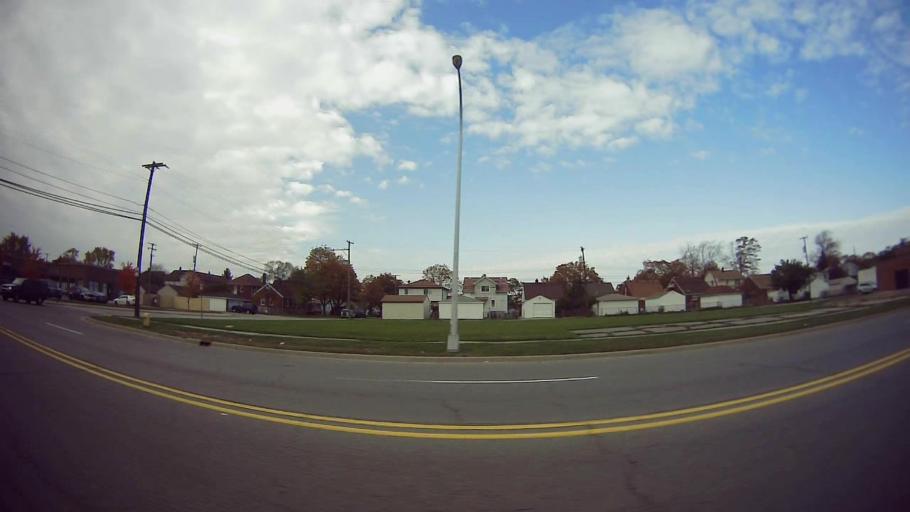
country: US
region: Michigan
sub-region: Wayne County
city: Dearborn
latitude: 42.3512
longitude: -83.1773
